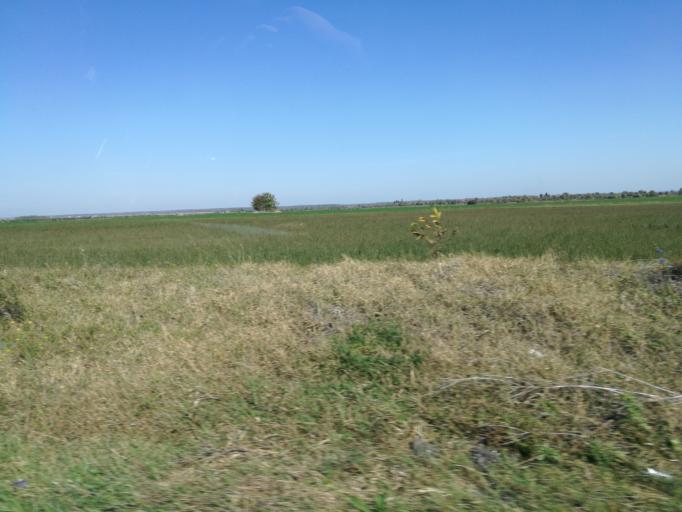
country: RO
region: Giurgiu
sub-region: Comuna Joita
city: Bacu
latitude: 44.4797
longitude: 25.8990
